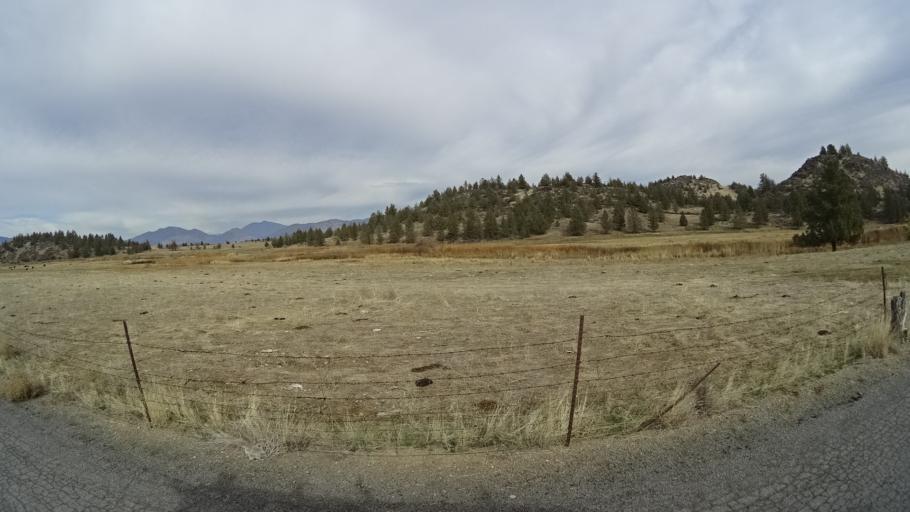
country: US
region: California
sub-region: Siskiyou County
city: Montague
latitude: 41.6834
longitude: -122.5191
